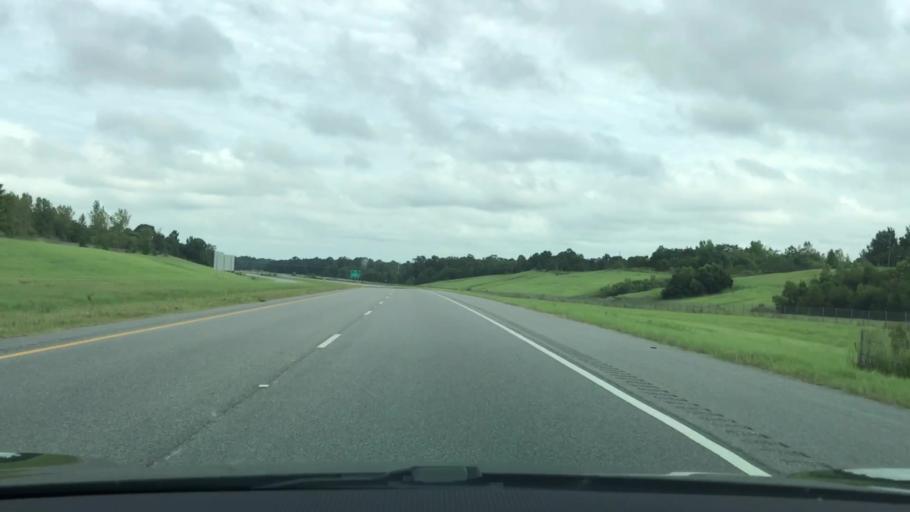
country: US
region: Alabama
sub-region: Montgomery County
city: Pike Road
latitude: 32.3478
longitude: -86.0649
